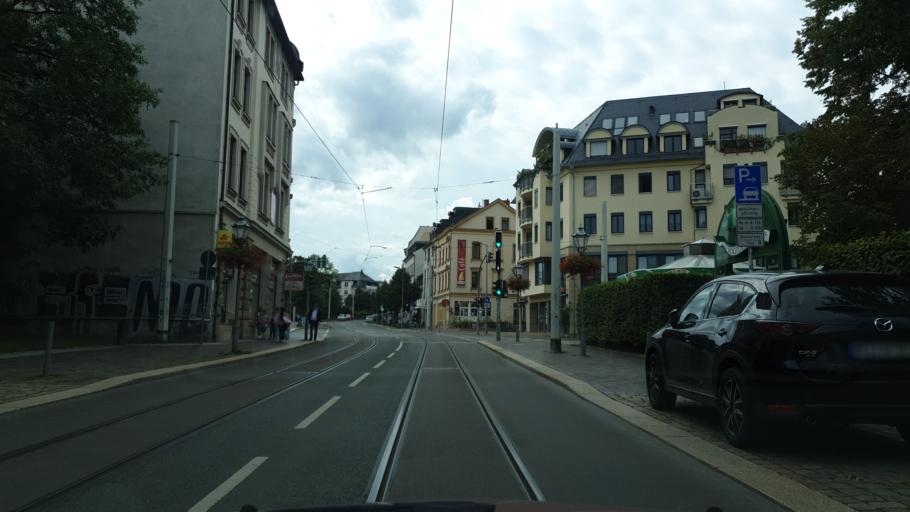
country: DE
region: Saxony
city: Plauen
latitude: 50.4949
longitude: 12.1321
